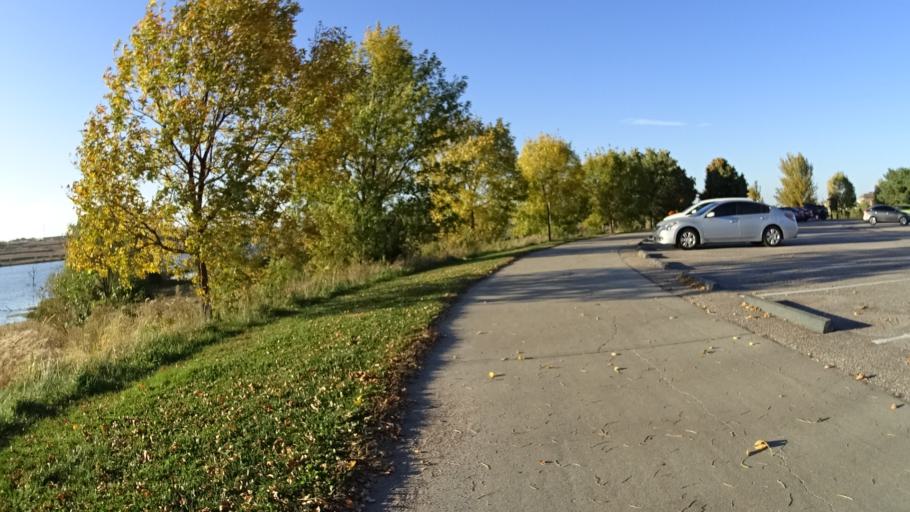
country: US
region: Nebraska
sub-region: Sarpy County
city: Papillion
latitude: 41.1395
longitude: -96.0654
